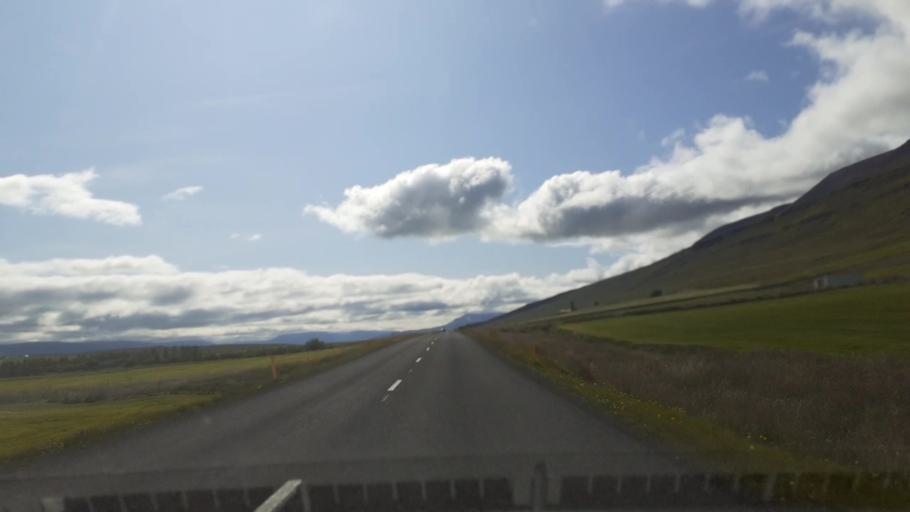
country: IS
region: Northeast
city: Akureyri
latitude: 65.8653
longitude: -18.2618
